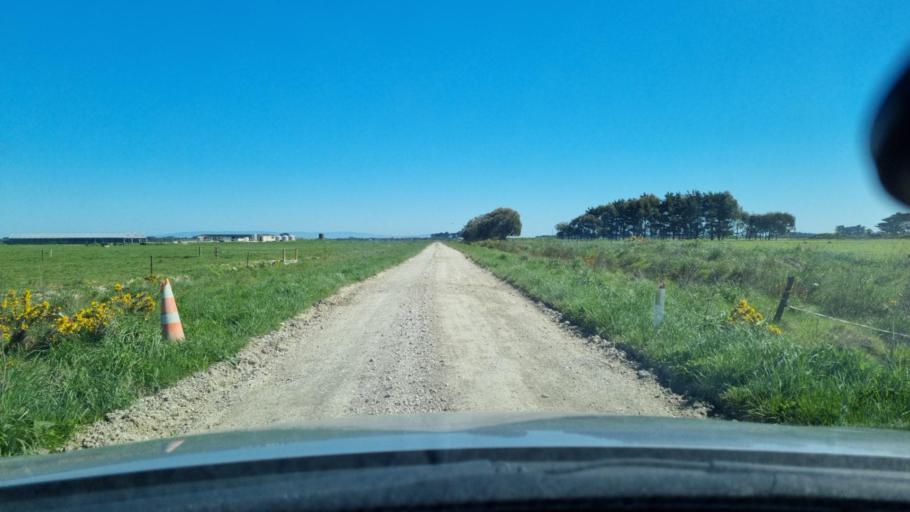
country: NZ
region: Southland
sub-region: Invercargill City
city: Invercargill
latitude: -46.4236
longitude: 168.3144
